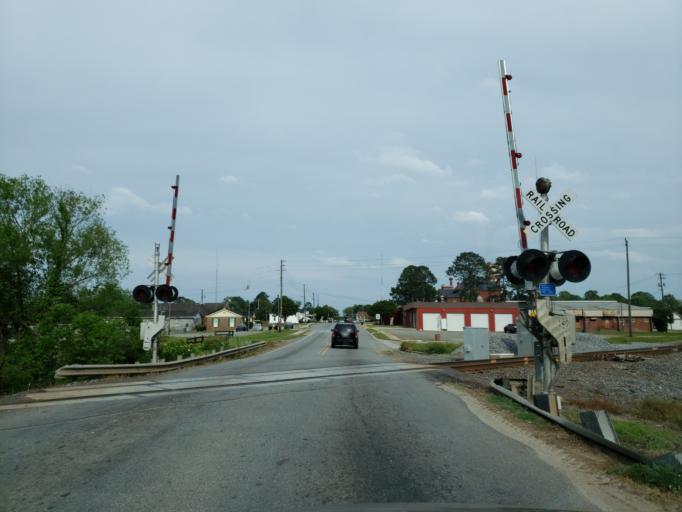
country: US
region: Georgia
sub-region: Dooly County
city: Vienna
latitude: 32.0919
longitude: -83.7998
